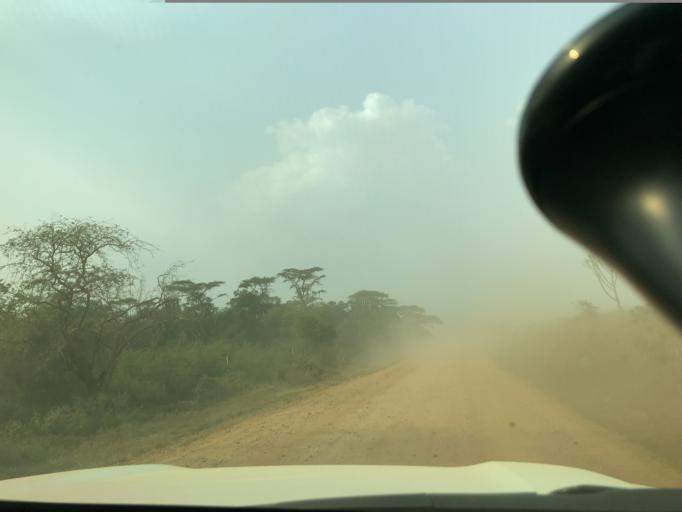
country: CD
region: Nord Kivu
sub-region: North Kivu
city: Butembo
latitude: 0.1040
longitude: 29.6402
